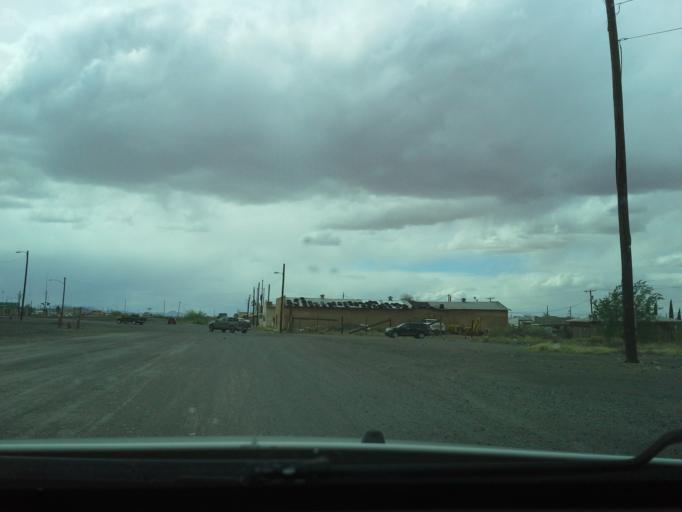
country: US
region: New Mexico
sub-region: Hidalgo County
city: Lordsburg
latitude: 32.3503
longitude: -108.7053
